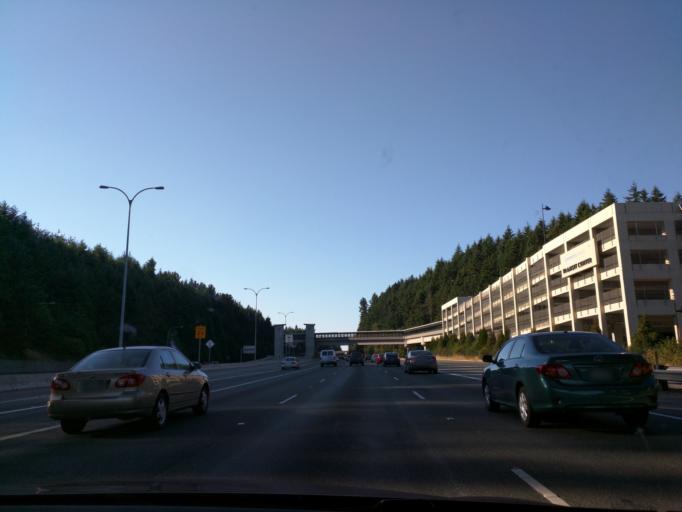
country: US
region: Washington
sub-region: Snohomish County
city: Mountlake Terrace
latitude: 47.7849
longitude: -122.3161
